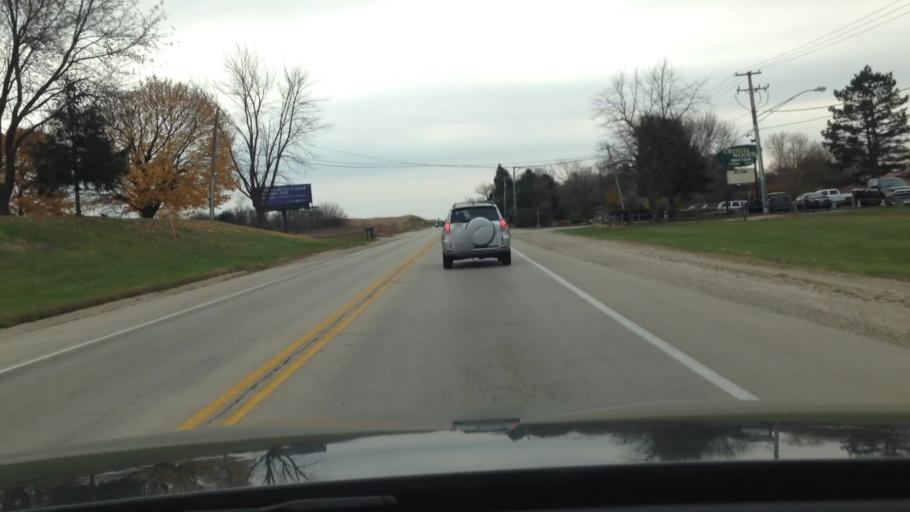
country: US
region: Illinois
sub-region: McHenry County
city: Lakewood
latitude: 42.2425
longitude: -88.4226
